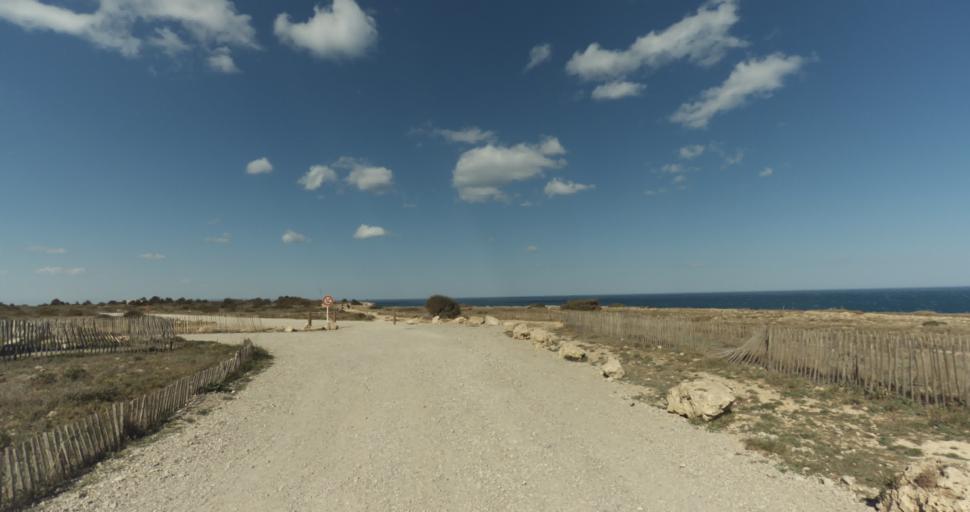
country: FR
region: Languedoc-Roussillon
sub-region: Departement de l'Aude
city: Leucate
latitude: 42.9114
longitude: 3.0573
